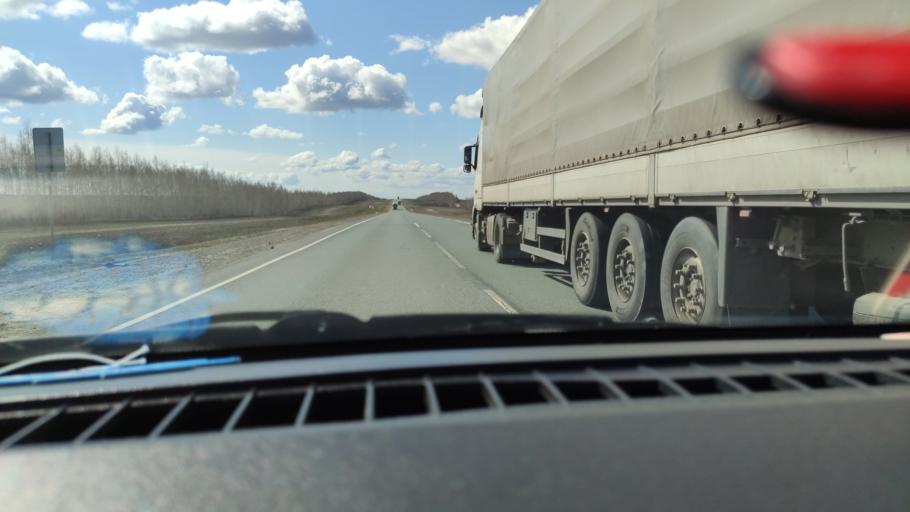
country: RU
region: Samara
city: Syzran'
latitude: 52.9140
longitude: 48.3005
